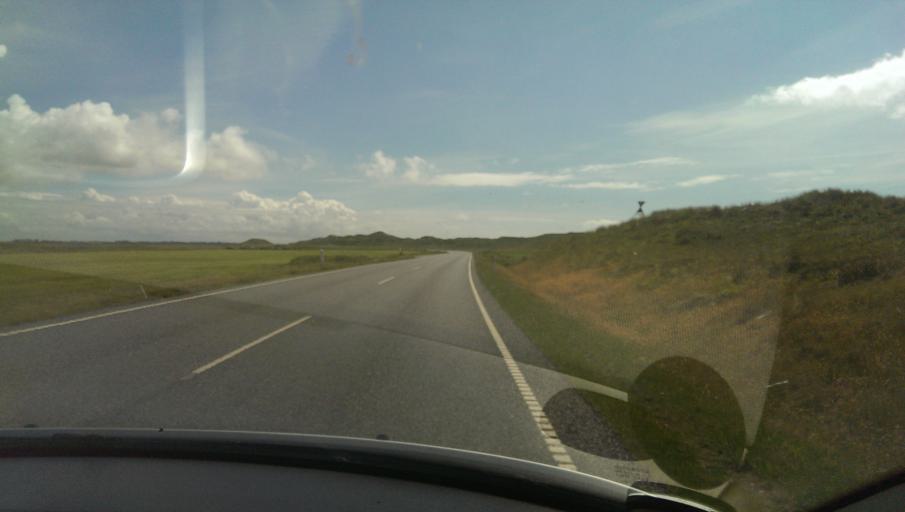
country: DK
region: Central Jutland
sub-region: Ringkobing-Skjern Kommune
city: Ringkobing
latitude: 56.1807
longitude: 8.1275
